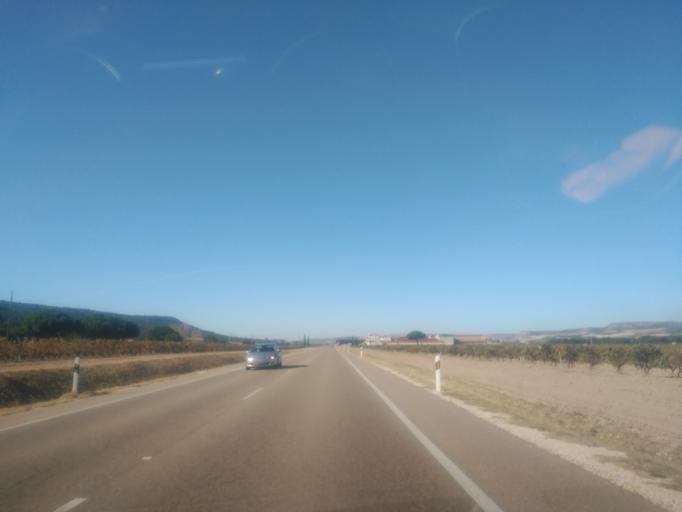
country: ES
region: Castille and Leon
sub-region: Provincia de Valladolid
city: Valbuena de Duero
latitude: 41.6280
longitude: -4.3129
